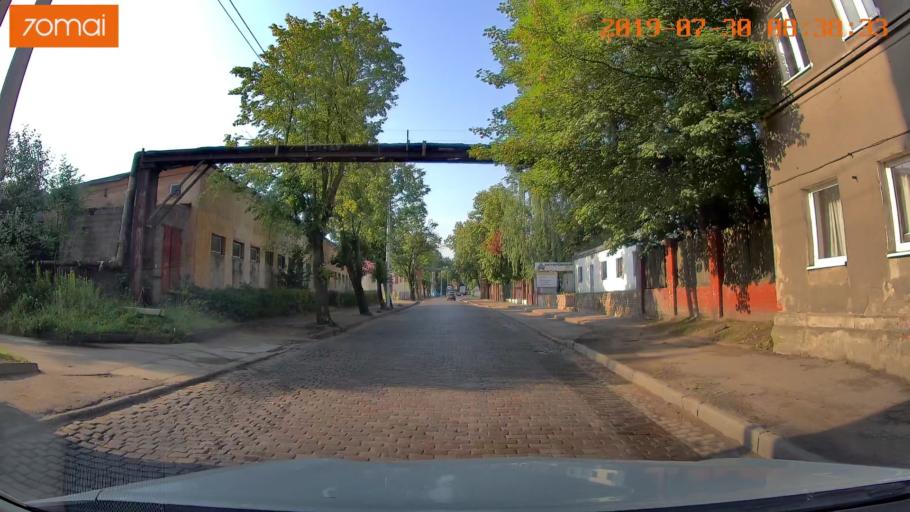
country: RU
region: Kaliningrad
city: Chernyakhovsk
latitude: 54.6345
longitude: 21.8030
